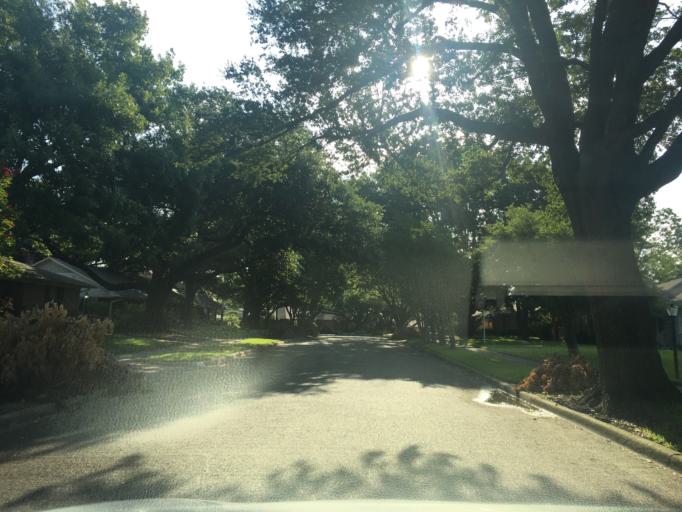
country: US
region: Texas
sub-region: Dallas County
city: Highland Park
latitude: 32.8451
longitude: -96.7586
